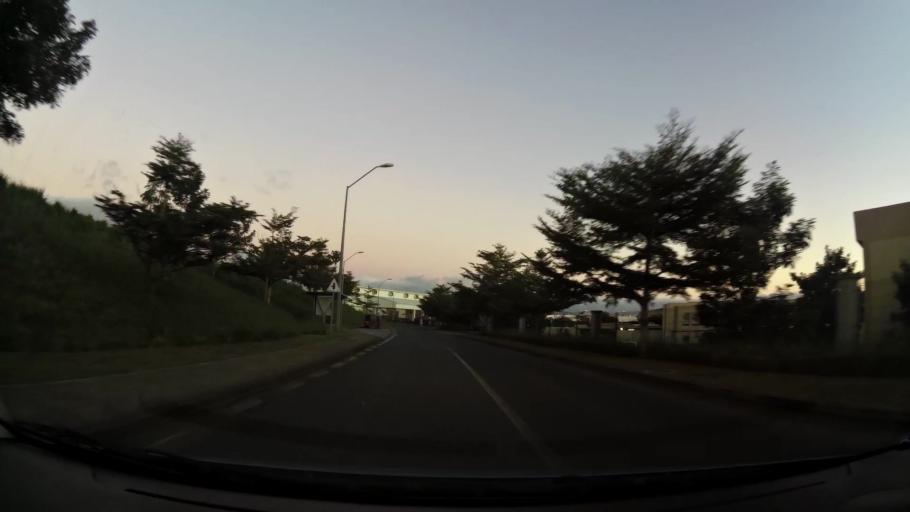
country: MU
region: Moka
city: Moka
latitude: -20.2247
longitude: 57.4983
